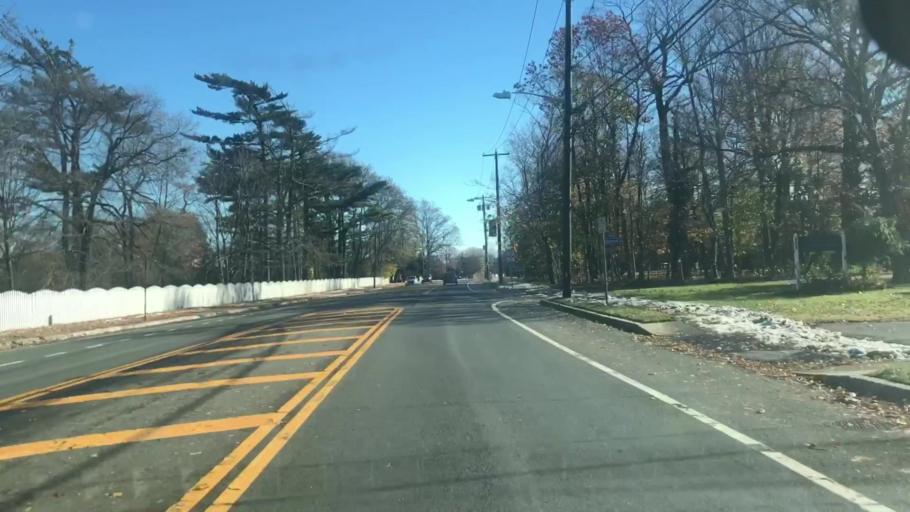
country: US
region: New York
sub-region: Suffolk County
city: West Islip
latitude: 40.6967
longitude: -73.3063
